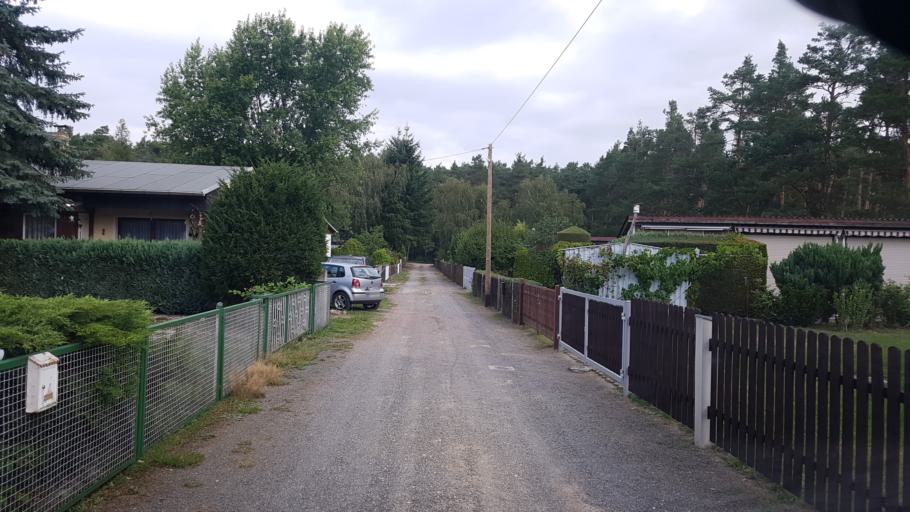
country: DE
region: Brandenburg
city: Ruckersdorf
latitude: 51.5757
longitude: 13.5783
